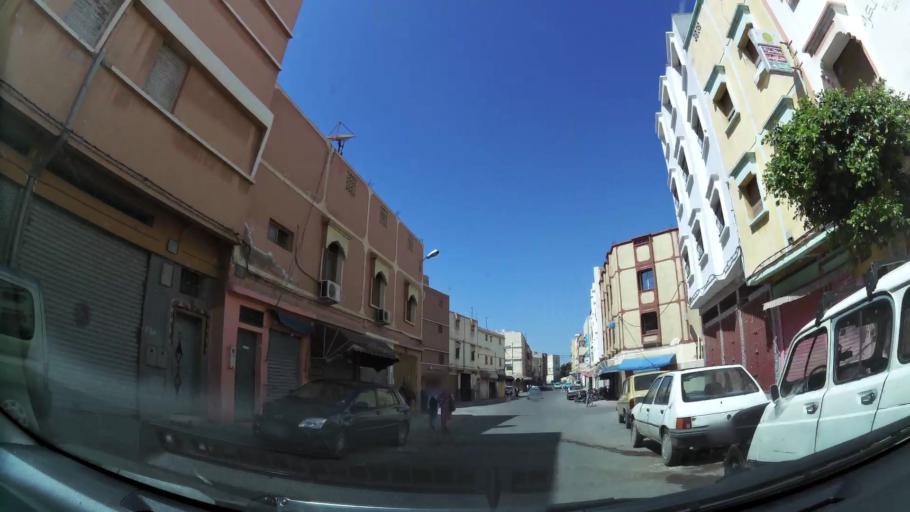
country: MA
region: Souss-Massa-Draa
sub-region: Inezgane-Ait Mellou
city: Inezgane
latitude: 30.3492
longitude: -9.5379
